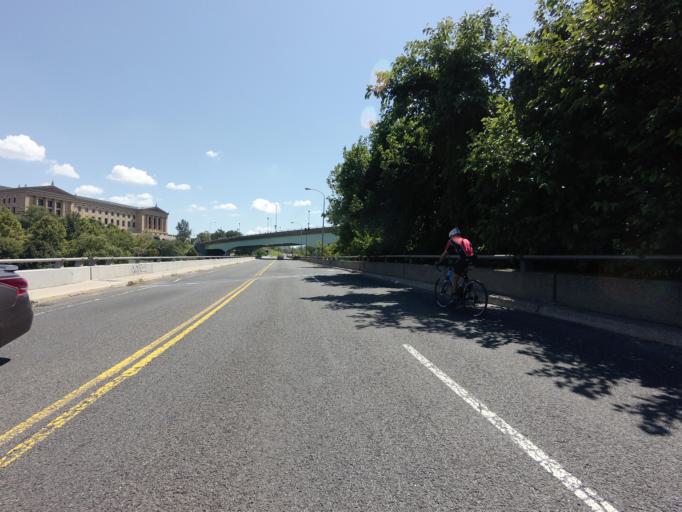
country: US
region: Pennsylvania
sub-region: Philadelphia County
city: Philadelphia
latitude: 39.9647
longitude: -75.1845
